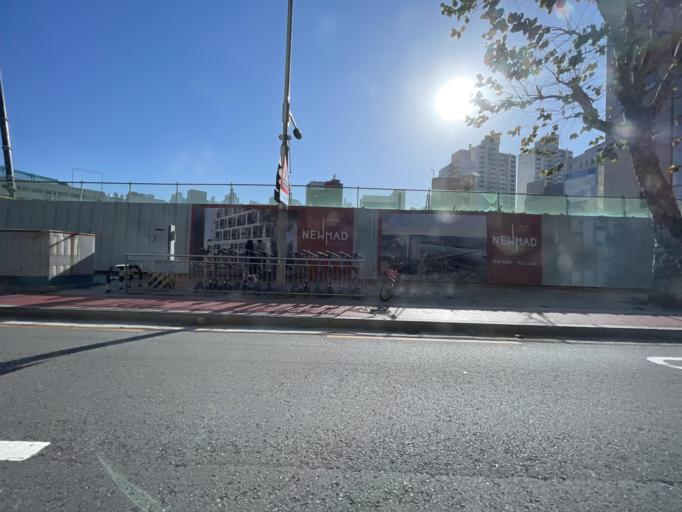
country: KR
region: Seoul
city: Seoul
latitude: 37.5389
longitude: 126.9454
